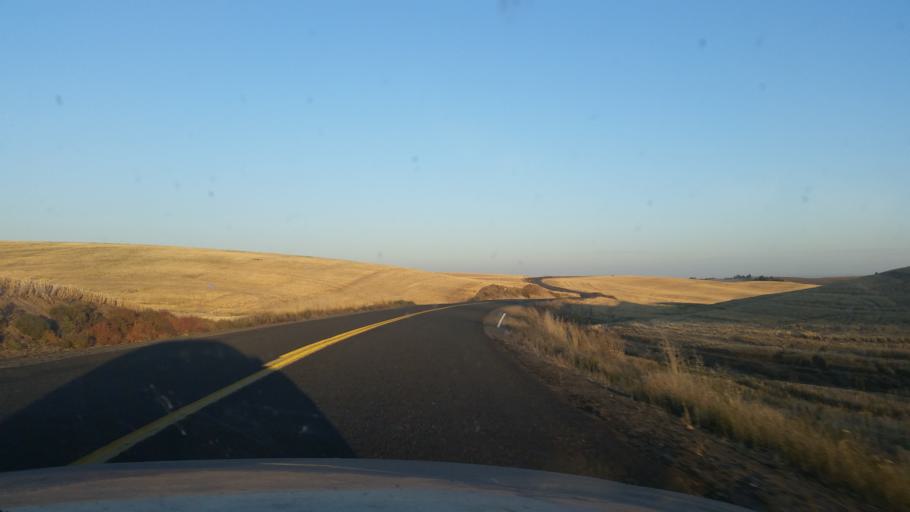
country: US
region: Washington
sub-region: Spokane County
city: Cheney
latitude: 47.5304
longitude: -117.6115
